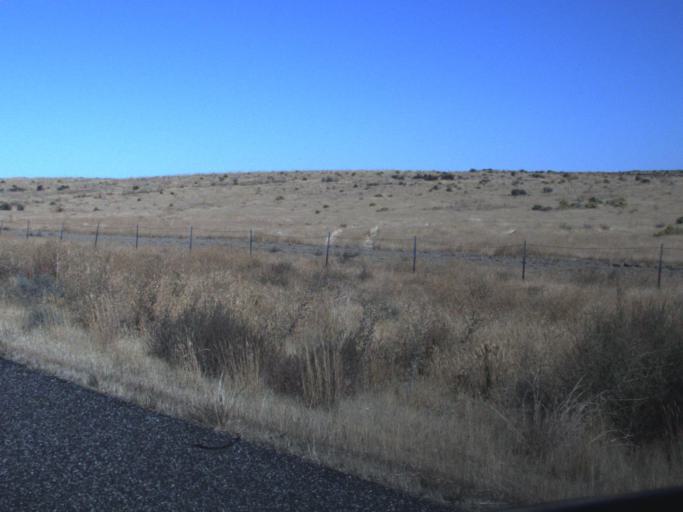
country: US
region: Washington
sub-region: Benton County
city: Benton City
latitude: 46.4544
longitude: -119.5146
